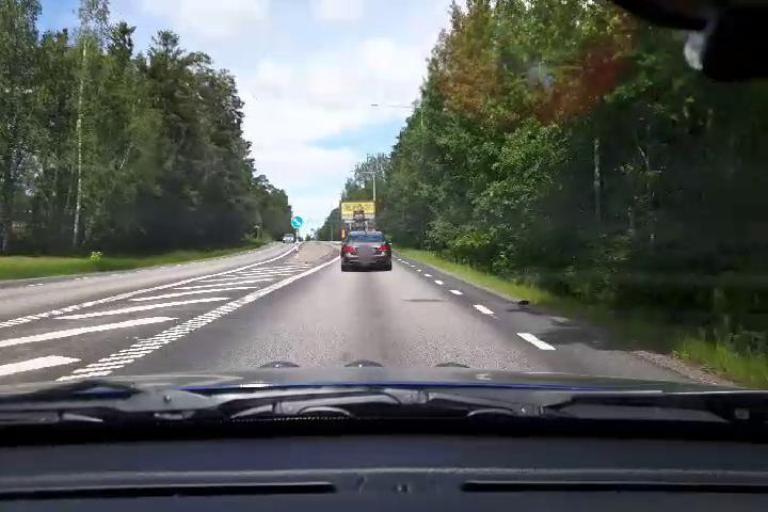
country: SE
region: Uppsala
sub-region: Osthammars Kommun
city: Bjorklinge
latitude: 60.0400
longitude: 17.5507
